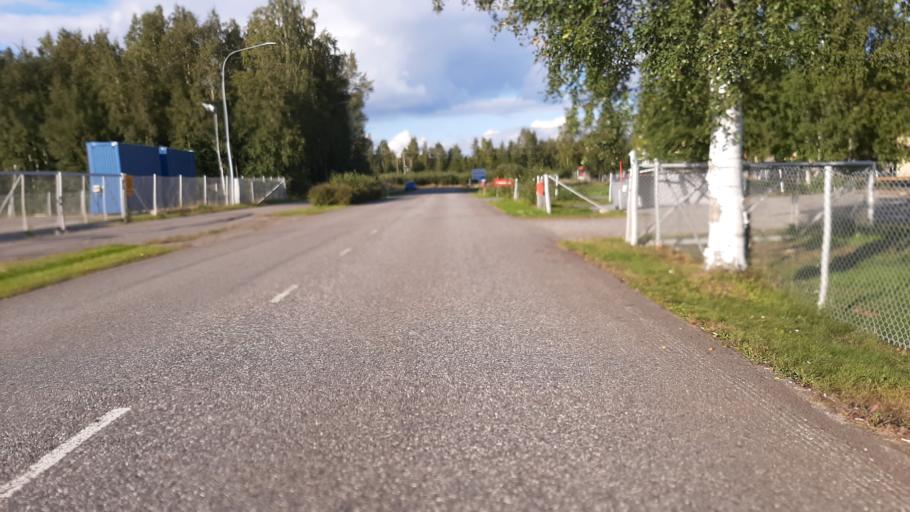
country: FI
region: North Karelia
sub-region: Joensuu
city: Joensuu
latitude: 62.6287
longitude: 29.8017
